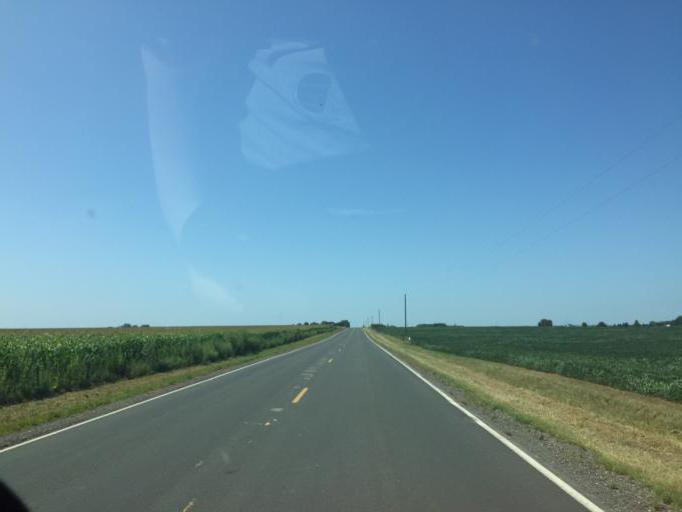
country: US
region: Minnesota
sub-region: Olmsted County
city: Rochester
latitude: 43.9640
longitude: -92.5094
